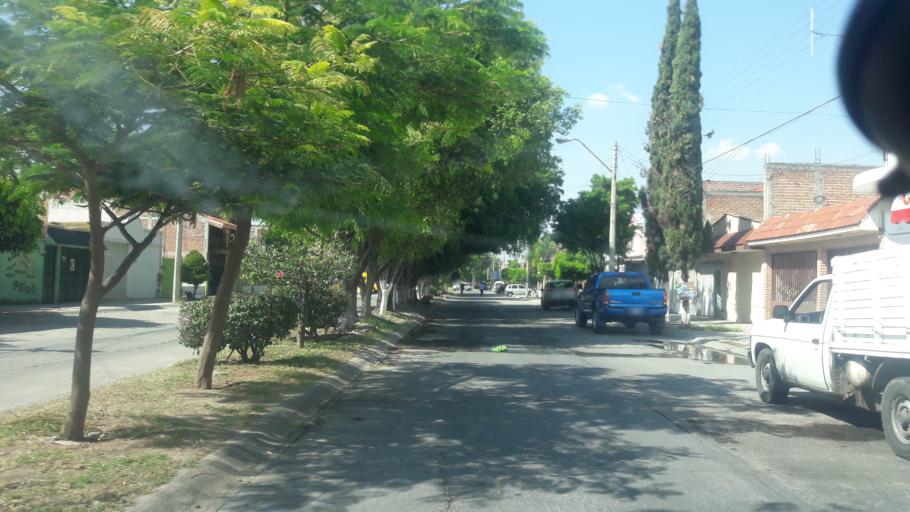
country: MX
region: Guanajuato
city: Leon
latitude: 21.1803
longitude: -101.6657
